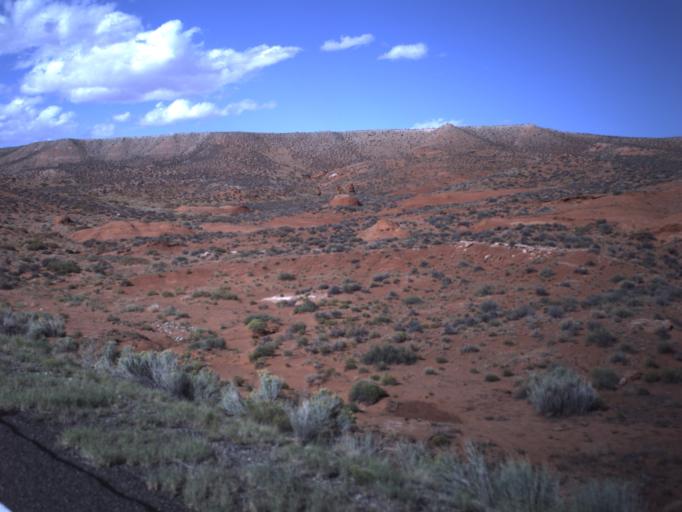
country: US
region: Utah
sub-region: Wayne County
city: Loa
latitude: 38.0711
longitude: -110.6070
